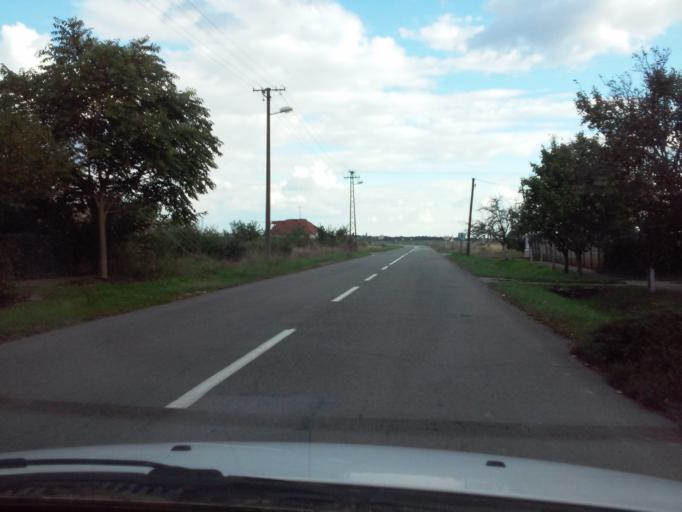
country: RS
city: Sajan
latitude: 45.8366
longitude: 20.2859
